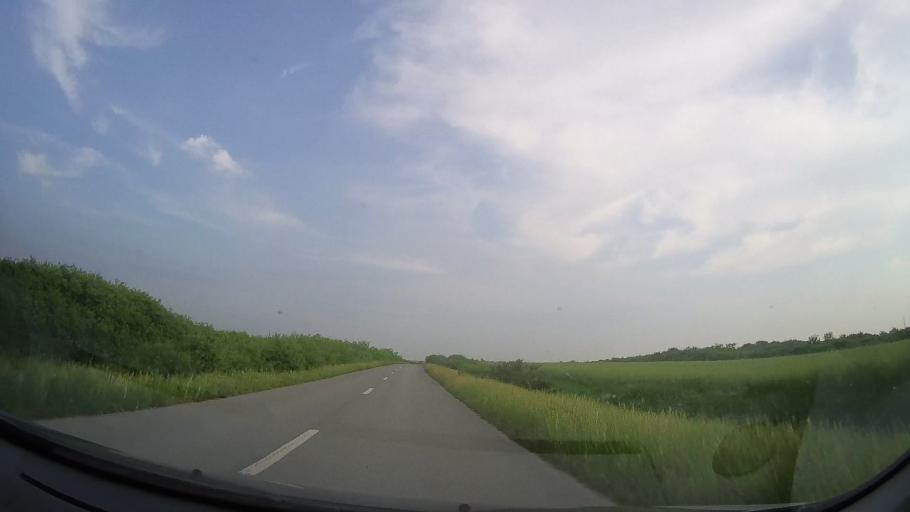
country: RO
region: Timis
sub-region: Comuna Foeni
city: Foeni
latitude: 45.4832
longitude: 20.8437
